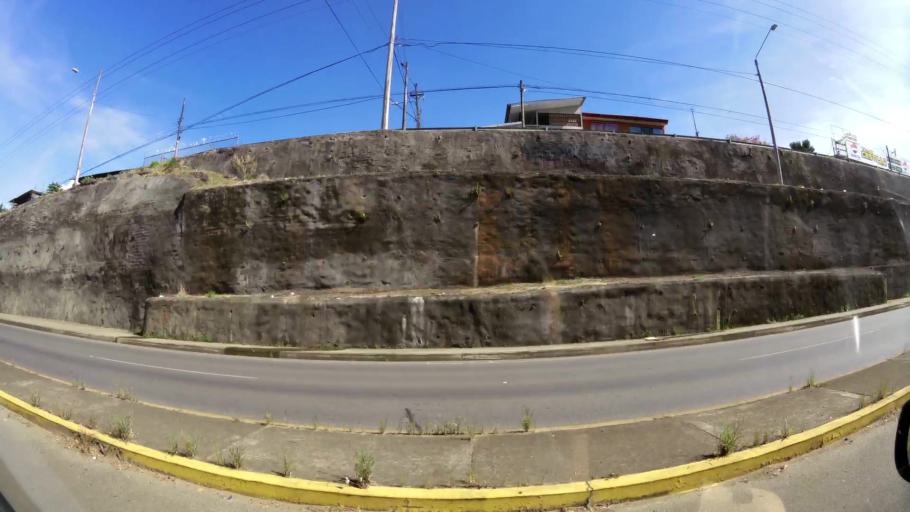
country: CR
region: San Jose
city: San Isidro
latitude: 9.3627
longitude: -83.6915
